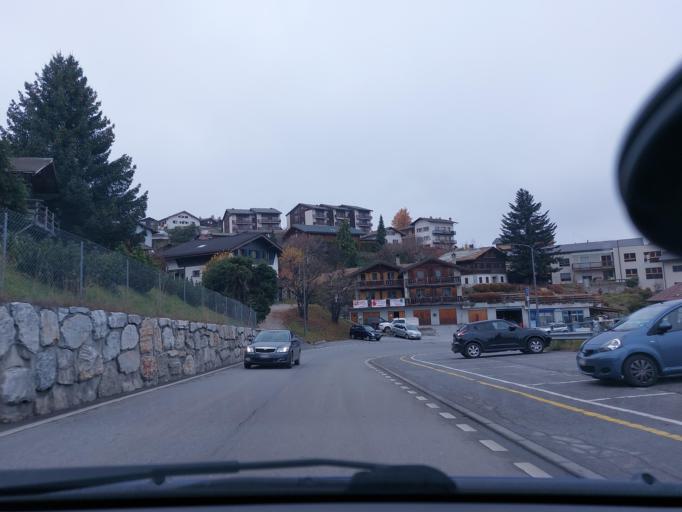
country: CH
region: Valais
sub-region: Conthey District
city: Basse-Nendaz
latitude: 46.1846
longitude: 7.2987
